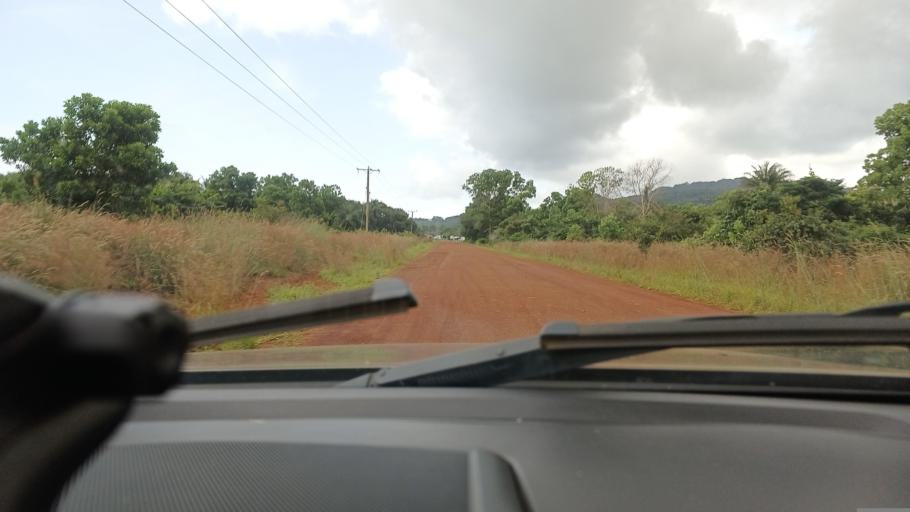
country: LR
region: Grand Cape Mount
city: Robertsport
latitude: 6.7049
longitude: -11.3286
